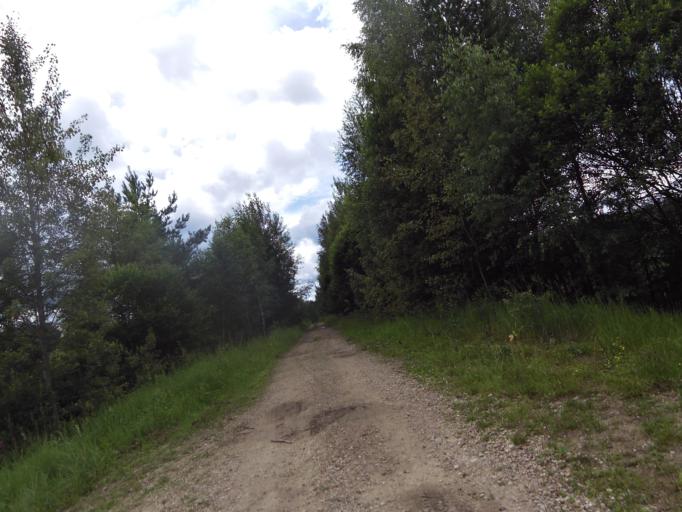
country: RU
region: Moskovskaya
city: Danki
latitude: 54.9462
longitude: 37.6905
